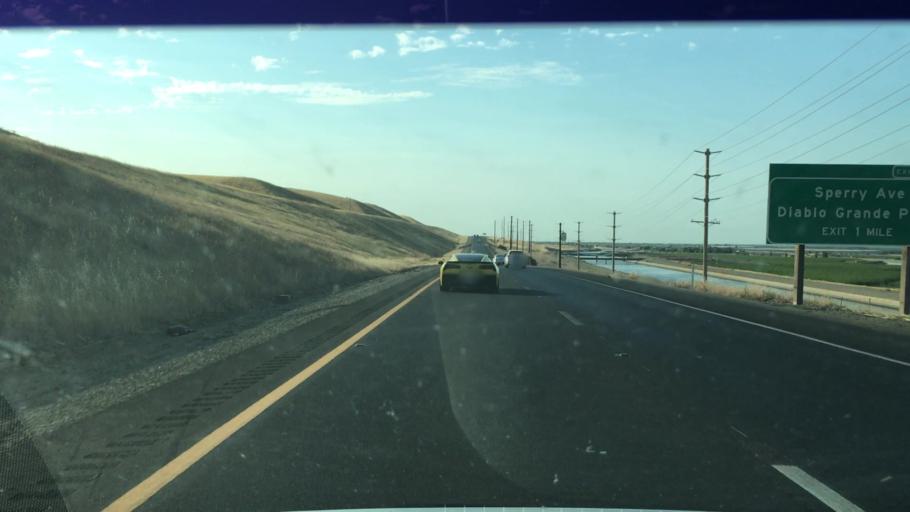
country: US
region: California
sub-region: Stanislaus County
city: Patterson
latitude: 37.4473
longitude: -121.1679
